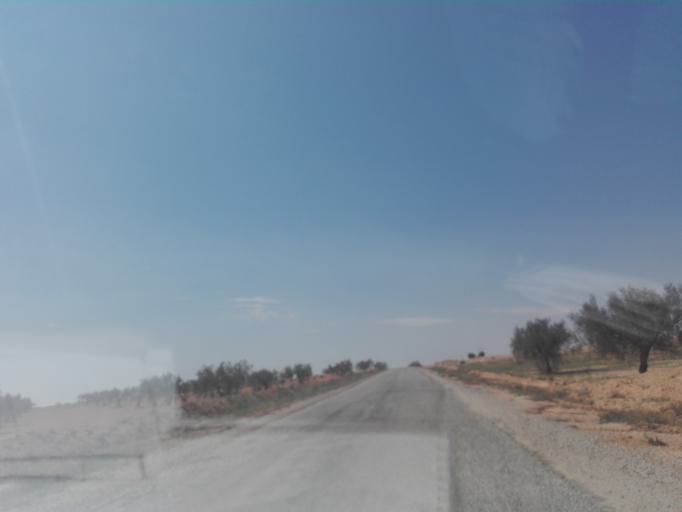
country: TN
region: Safaqis
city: Bi'r `Ali Bin Khalifah
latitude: 34.6427
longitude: 10.4087
